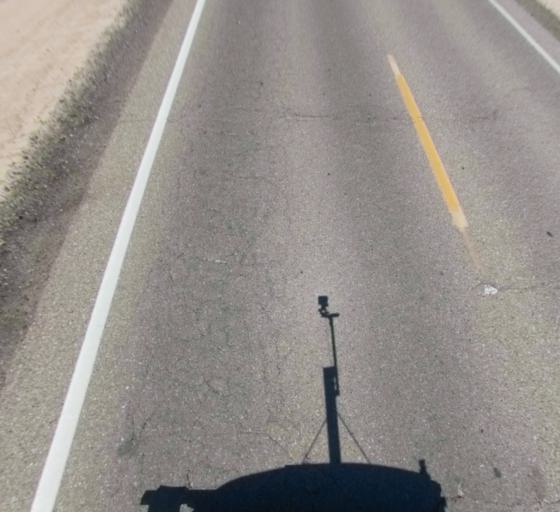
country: US
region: California
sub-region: Fresno County
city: Mendota
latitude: 36.8510
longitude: -120.3079
